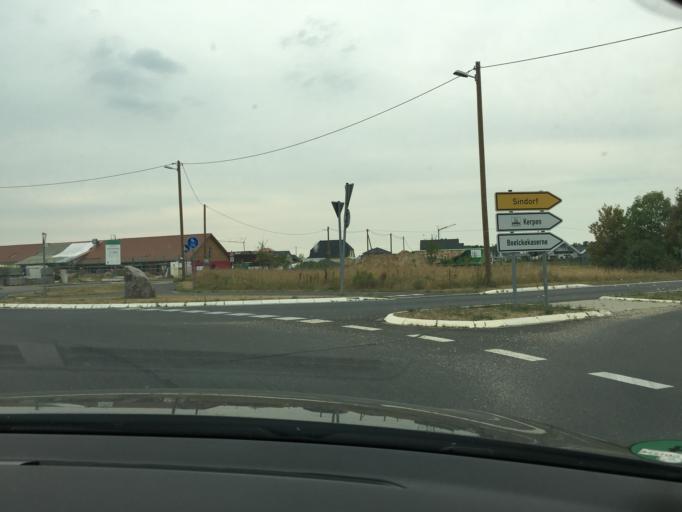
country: DE
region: North Rhine-Westphalia
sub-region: Regierungsbezirk Koln
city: Kerpen
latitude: 50.8673
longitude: 6.6662
